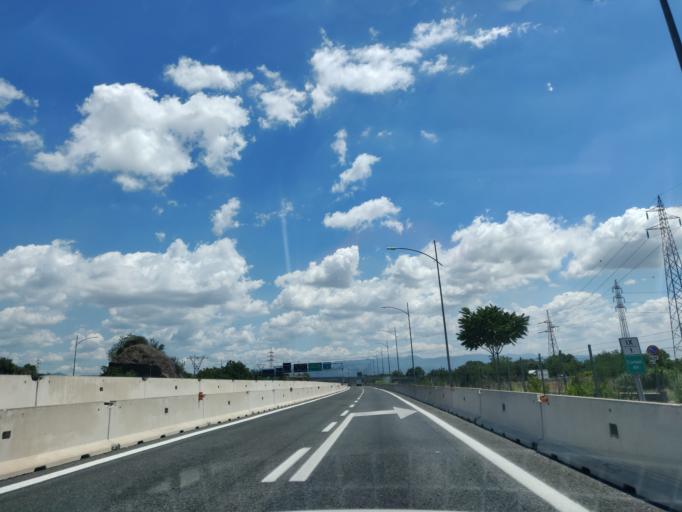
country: IT
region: Latium
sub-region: Citta metropolitana di Roma Capitale
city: Setteville
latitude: 41.9229
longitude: 12.6330
